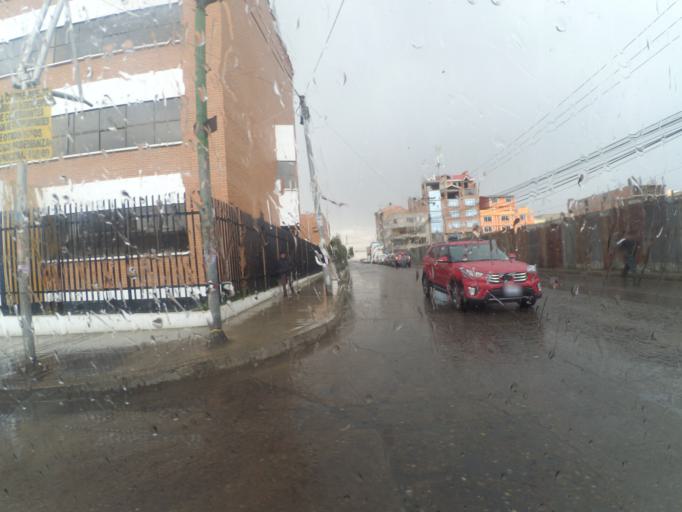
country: BO
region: La Paz
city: La Paz
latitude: -16.5177
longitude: -68.1659
